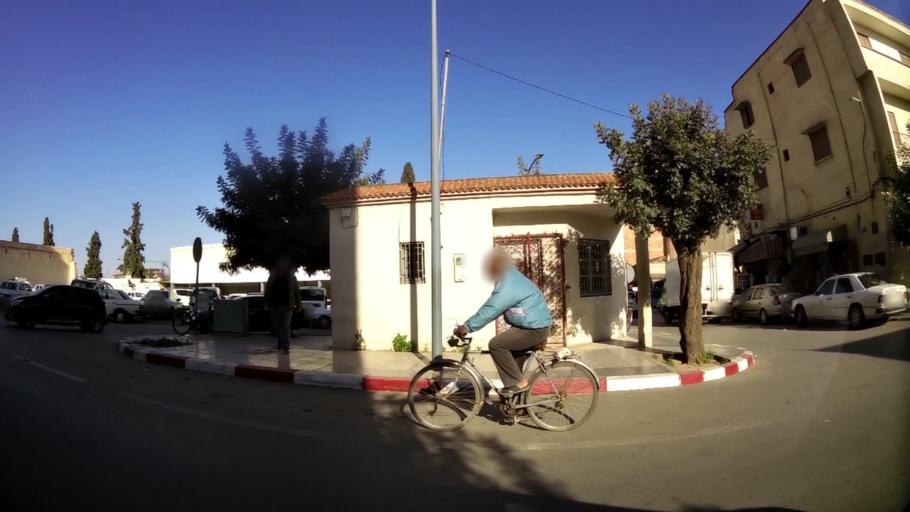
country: MA
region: Oriental
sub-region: Oujda-Angad
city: Oujda
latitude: 34.6882
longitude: -1.9152
